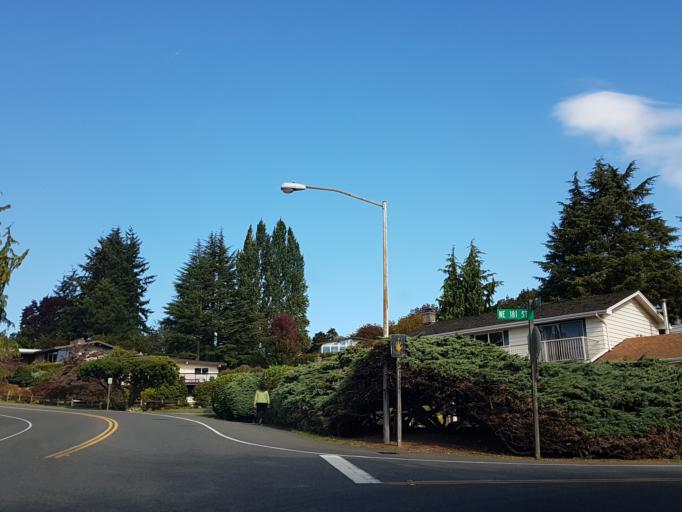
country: US
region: Washington
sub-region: King County
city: Lake Forest Park
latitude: 47.7591
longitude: -122.2638
